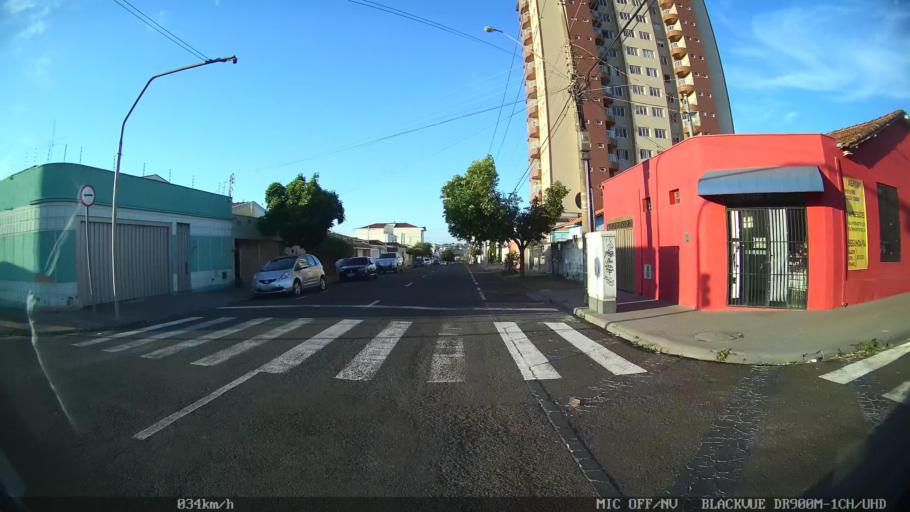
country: BR
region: Sao Paulo
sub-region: Franca
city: Franca
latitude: -20.5251
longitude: -47.3941
